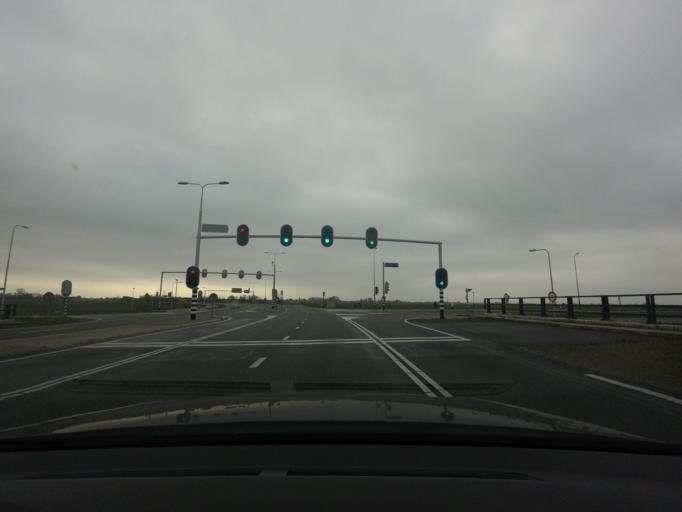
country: NL
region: North Holland
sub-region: Gemeente Uithoorn
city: Uithoorn
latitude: 52.2288
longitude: 4.8440
